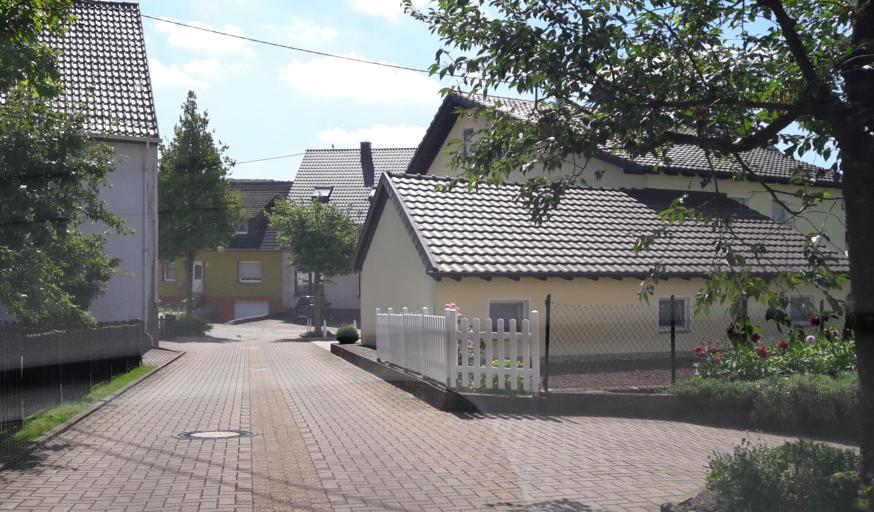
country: DE
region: Saarland
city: Freisen
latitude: 49.5569
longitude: 7.2505
